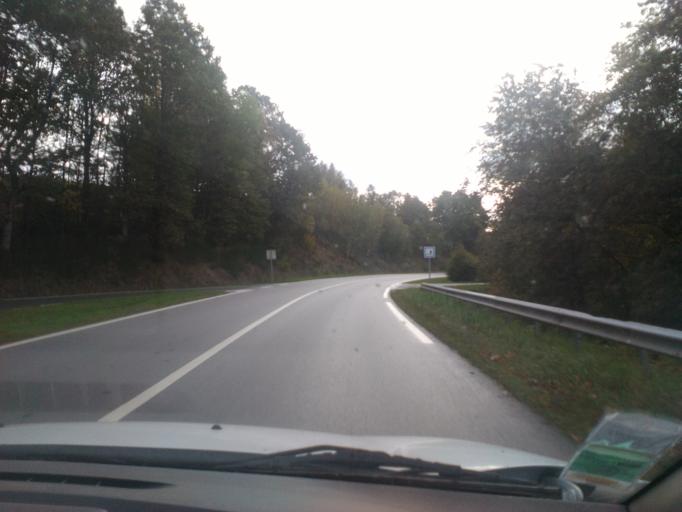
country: FR
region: Lorraine
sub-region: Departement des Vosges
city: Anould
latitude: 48.1597
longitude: 6.9198
